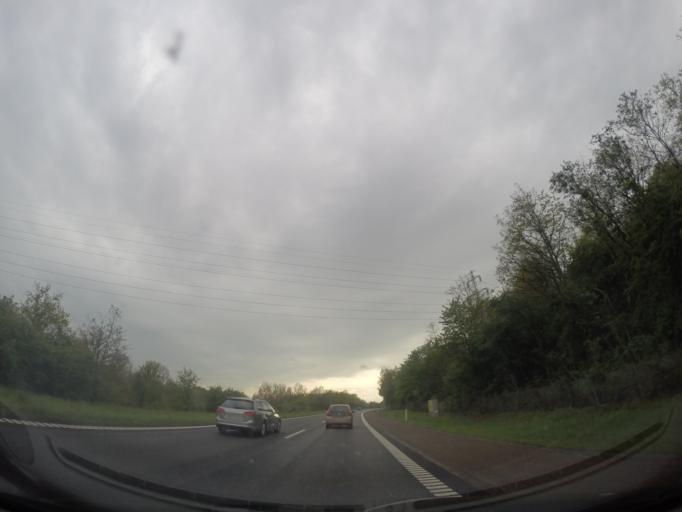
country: DK
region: Capital Region
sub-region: Hoje-Taastrup Kommune
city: Taastrup
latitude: 55.6662
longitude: 12.3097
